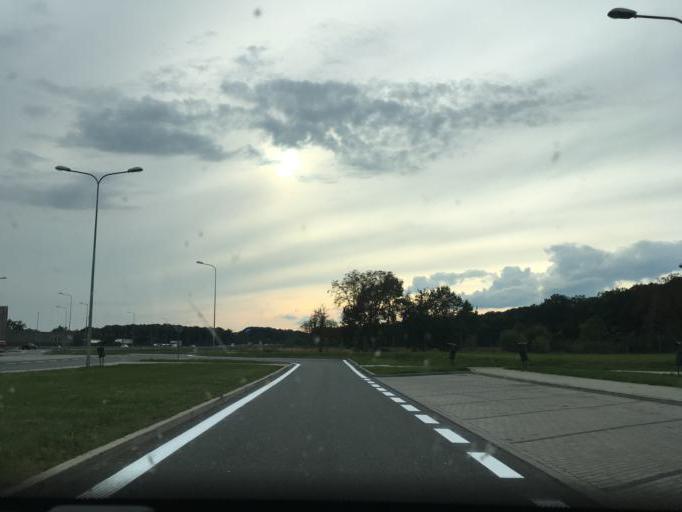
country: PL
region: Lower Silesian Voivodeship
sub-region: Powiat olesnicki
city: Sycow
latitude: 51.2968
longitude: 17.7397
